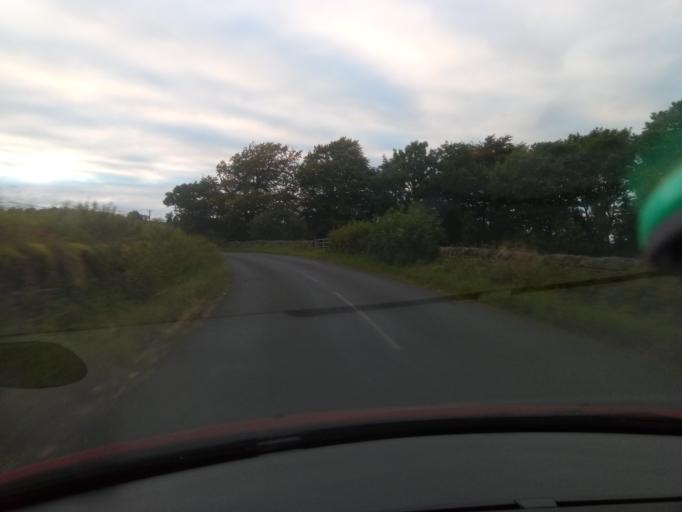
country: GB
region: England
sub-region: Northumberland
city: Bardon Mill
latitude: 54.9024
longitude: -2.3072
